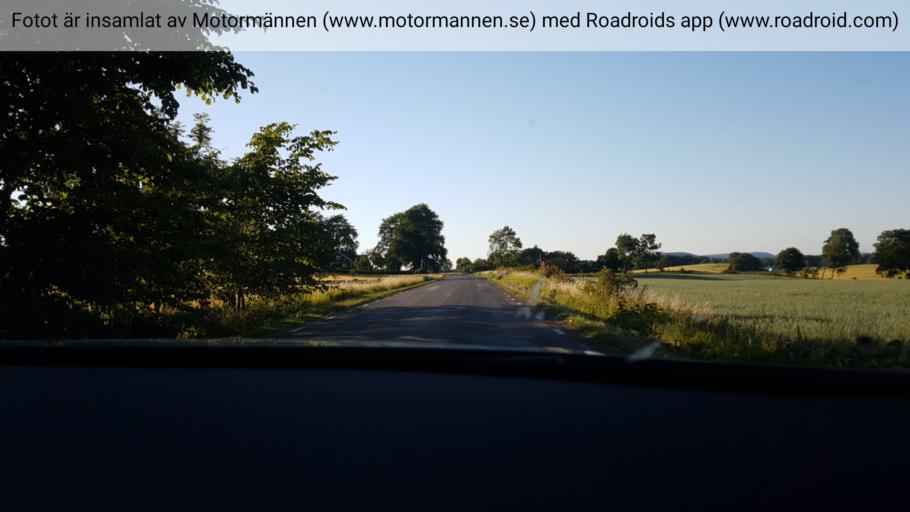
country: SE
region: Vaestra Goetaland
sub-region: Skovde Kommun
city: Skultorp
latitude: 58.2366
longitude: 13.7909
